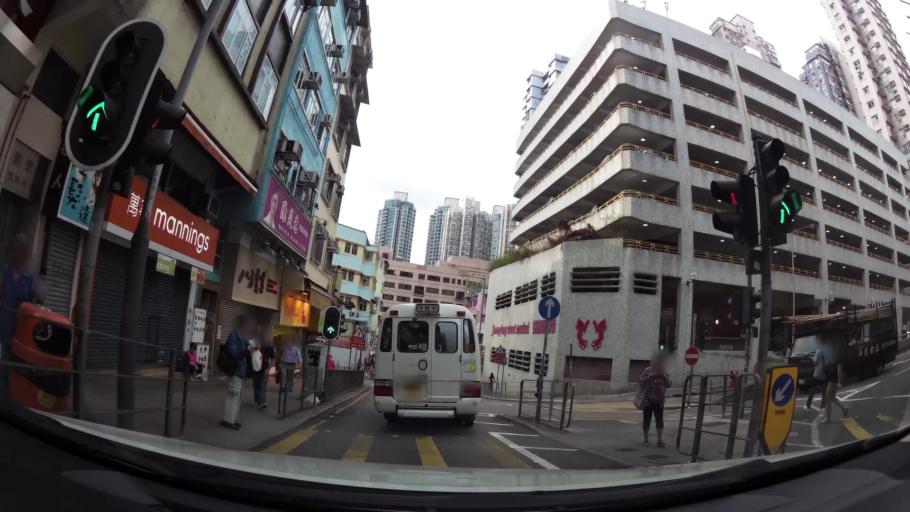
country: HK
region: Wong Tai Sin
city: Wong Tai Sin
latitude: 22.3442
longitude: 114.1975
